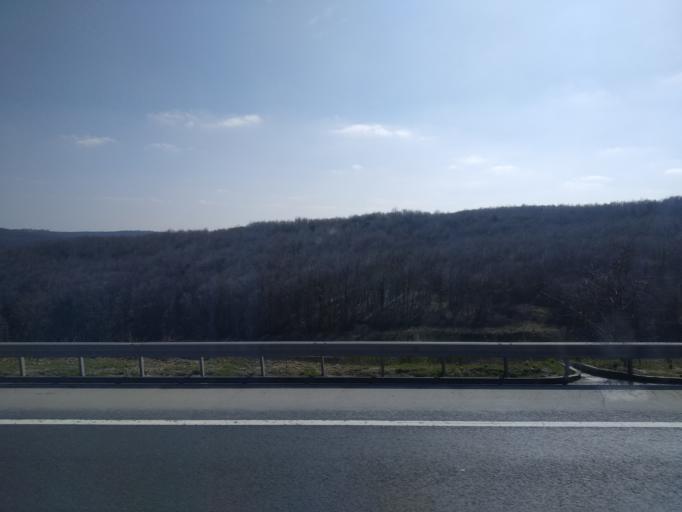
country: TR
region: Istanbul
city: Kemerburgaz
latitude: 41.2315
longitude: 28.8693
